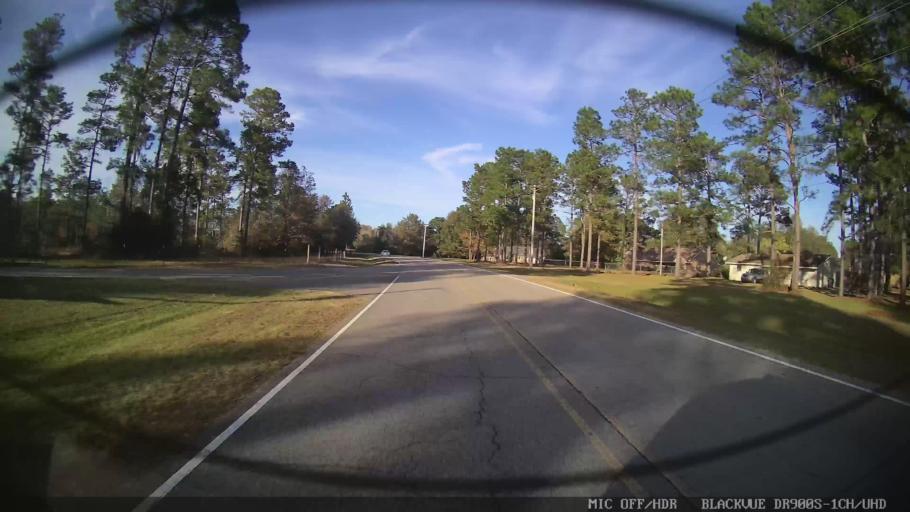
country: US
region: Mississippi
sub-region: Lamar County
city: Purvis
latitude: 31.1908
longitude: -89.2875
